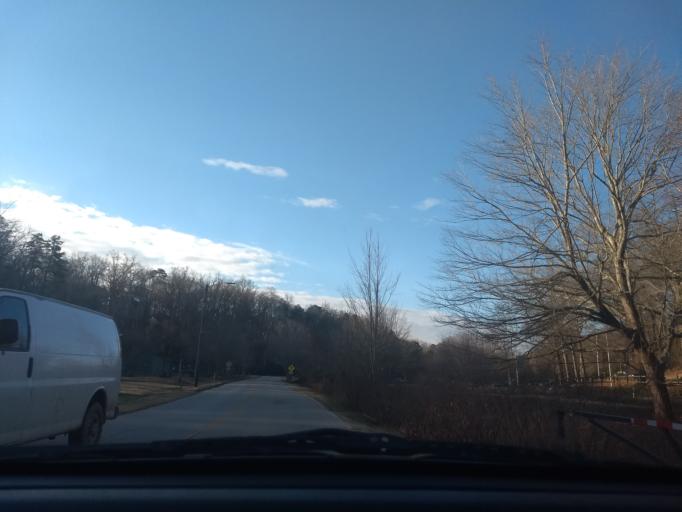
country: US
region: South Carolina
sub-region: Greenville County
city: Greenville
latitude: 34.8489
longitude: -82.3837
